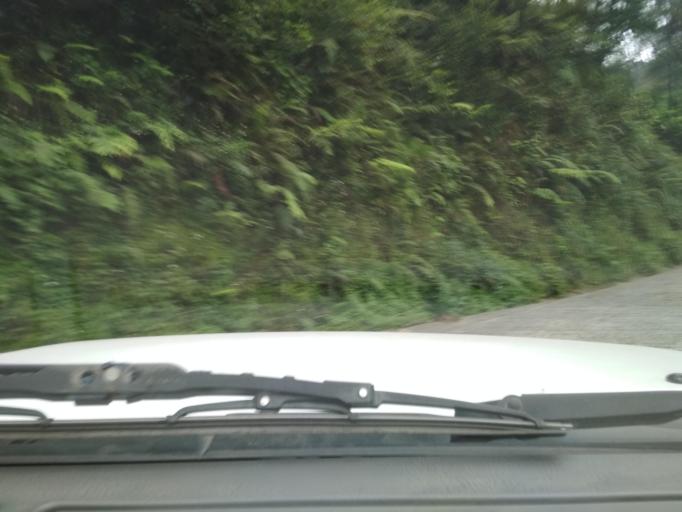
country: MX
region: Veracruz
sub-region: La Perla
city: Metlac Hernandez (Metlac Primero)
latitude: 18.9717
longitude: -97.1453
